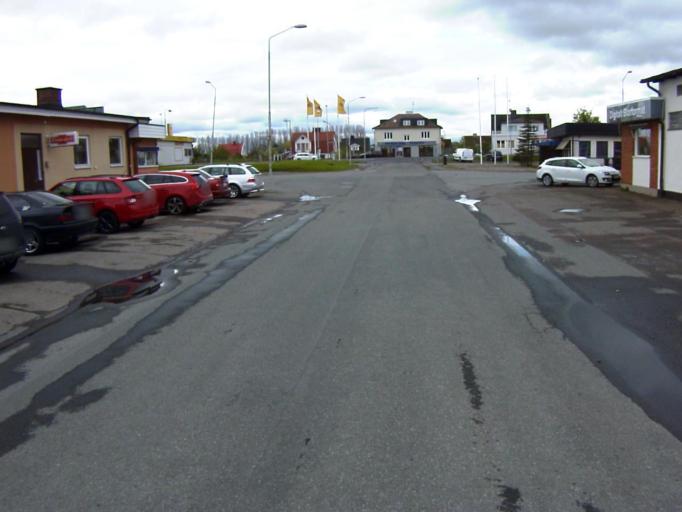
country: SE
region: Skane
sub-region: Kristianstads Kommun
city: Kristianstad
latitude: 56.0215
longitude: 14.1365
